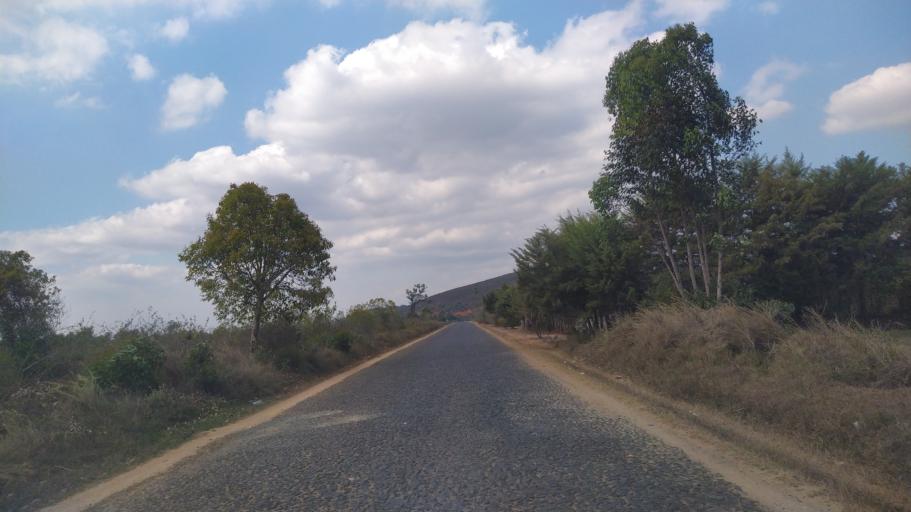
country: MG
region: Alaotra Mangoro
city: Moramanga
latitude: -18.7611
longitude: 48.2565
